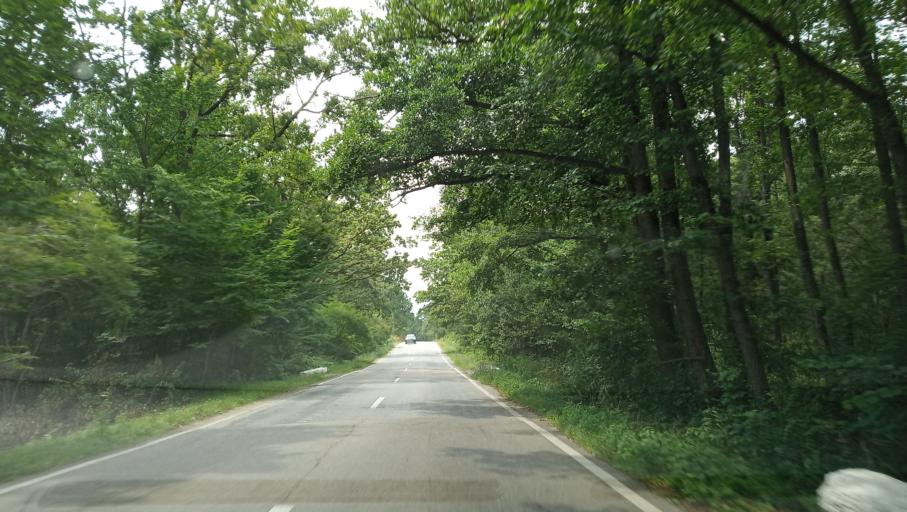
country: RO
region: Gorj
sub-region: Comuna Arcani
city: Arcani
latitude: 45.0890
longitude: 23.1097
